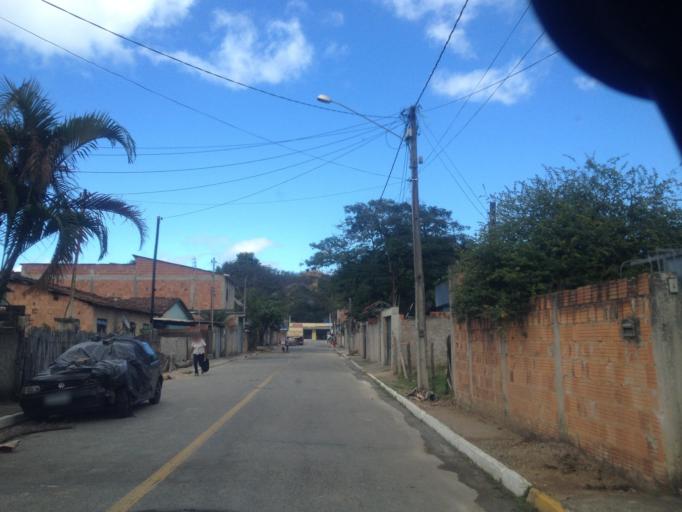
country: BR
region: Rio de Janeiro
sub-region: Porto Real
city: Porto Real
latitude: -22.4396
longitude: -44.3165
